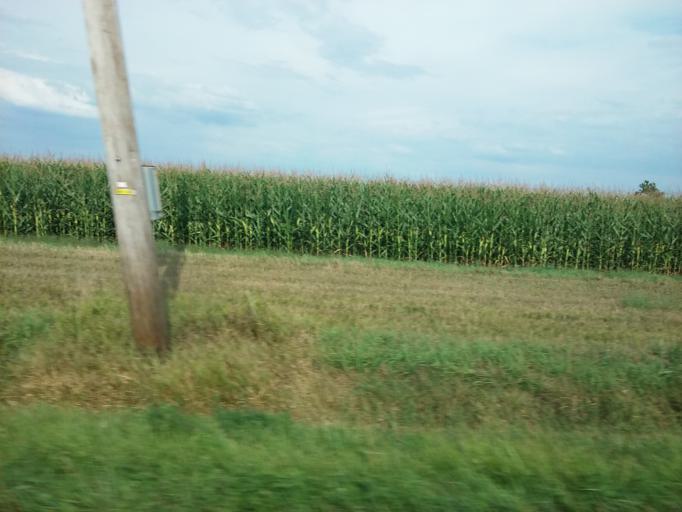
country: US
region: Ohio
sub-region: Hancock County
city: McComb
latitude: 41.1987
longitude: -83.7845
